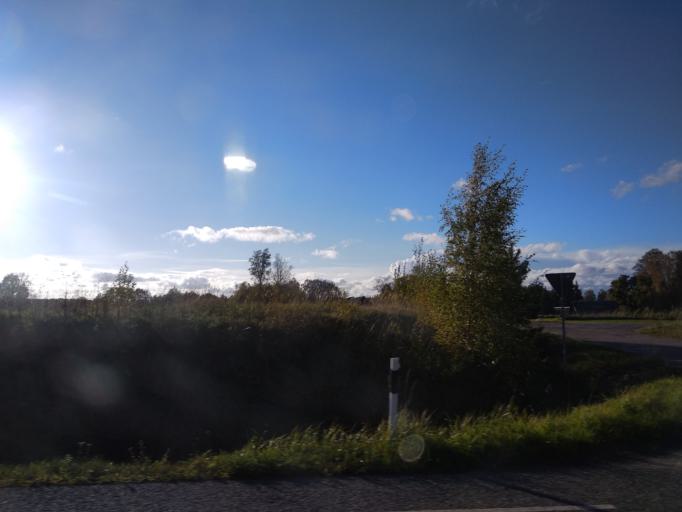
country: EE
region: Polvamaa
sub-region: Polva linn
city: Polva
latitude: 58.0177
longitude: 27.0618
